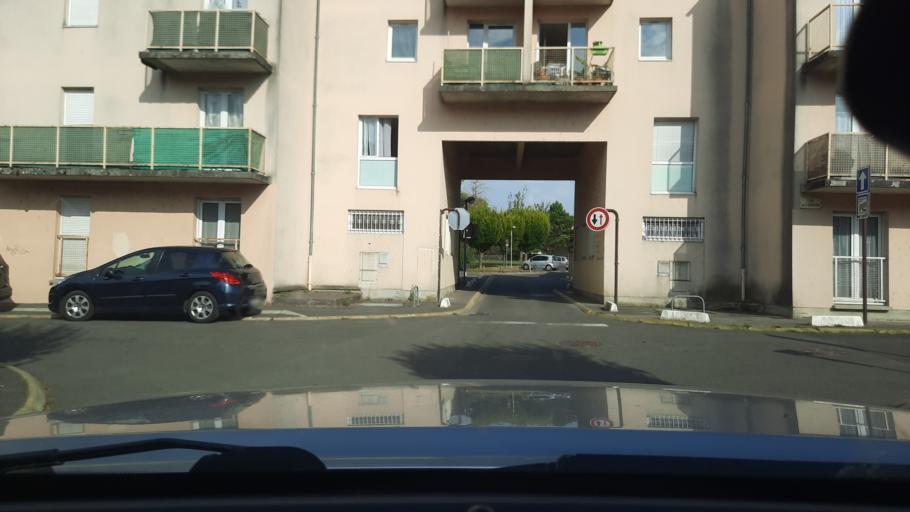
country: FR
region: Ile-de-France
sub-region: Departement de Seine-et-Marne
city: Ecuelles
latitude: 48.3647
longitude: 2.8281
